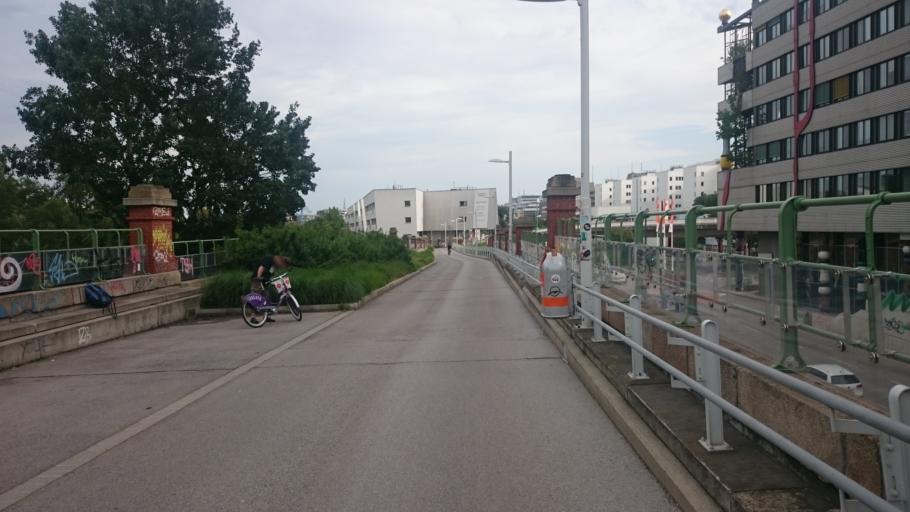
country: AT
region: Vienna
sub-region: Wien Stadt
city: Vienna
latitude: 48.2337
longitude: 16.3607
